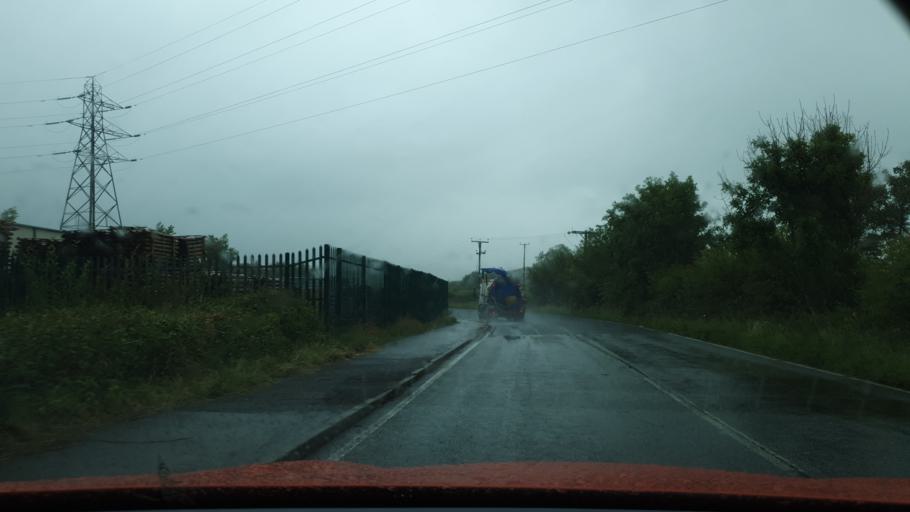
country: GB
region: England
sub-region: Cumbria
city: Millom
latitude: 54.2602
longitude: -3.2164
